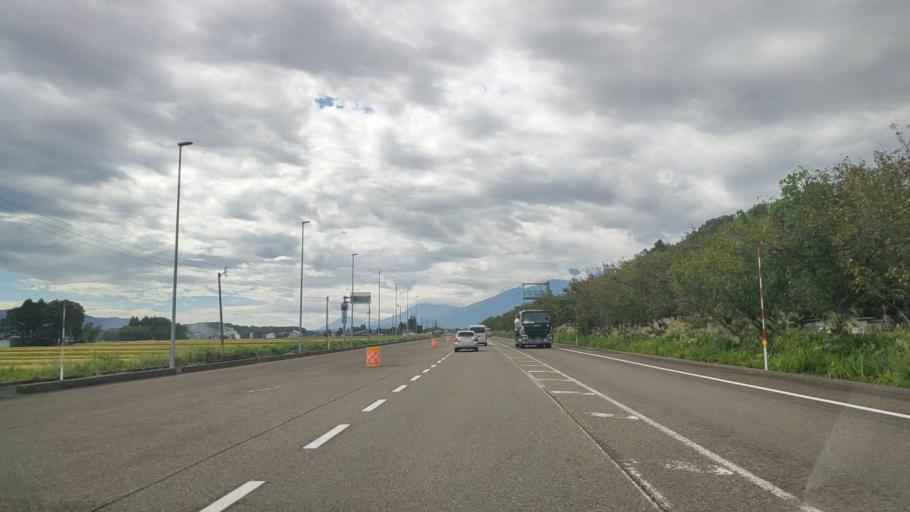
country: JP
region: Niigata
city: Arai
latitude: 37.0434
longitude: 138.2383
